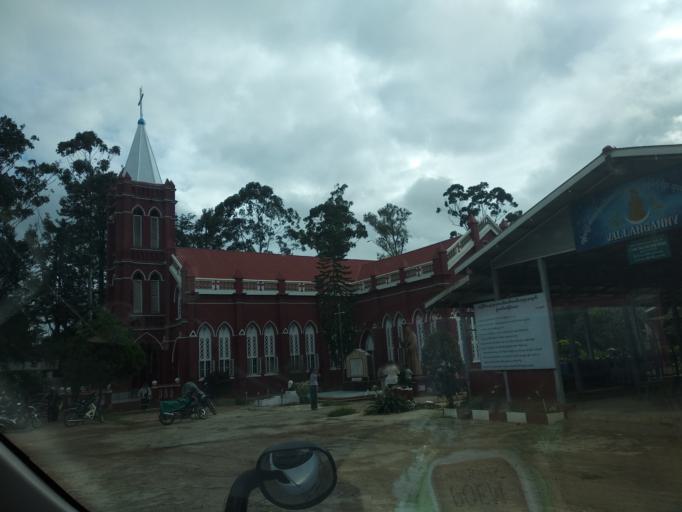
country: MM
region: Mandalay
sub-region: Pyin Oo Lwin District
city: Pyin Oo Lwin
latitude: 22.0254
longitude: 96.4712
